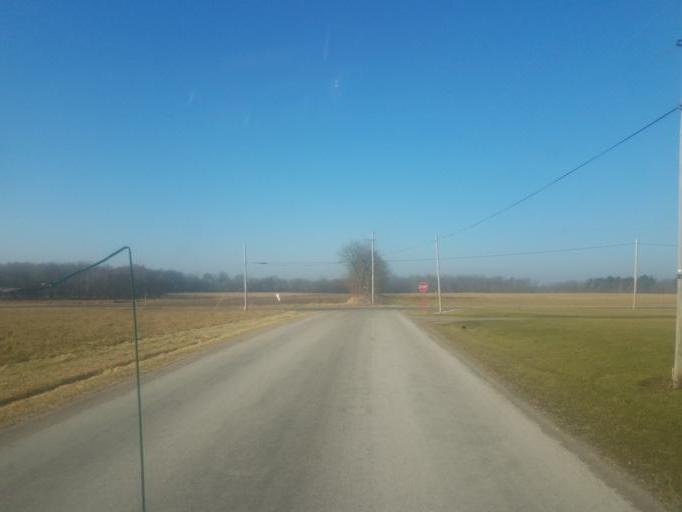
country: US
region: Ohio
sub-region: Crawford County
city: Bucyrus
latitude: 40.8995
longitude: -82.9559
